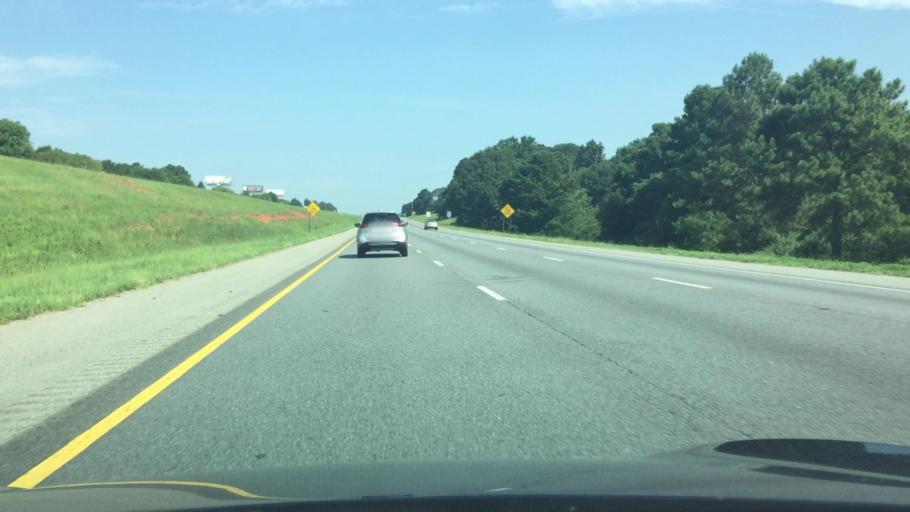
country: US
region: Alabama
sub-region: Elmore County
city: Millbrook
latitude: 32.4936
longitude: -86.4126
